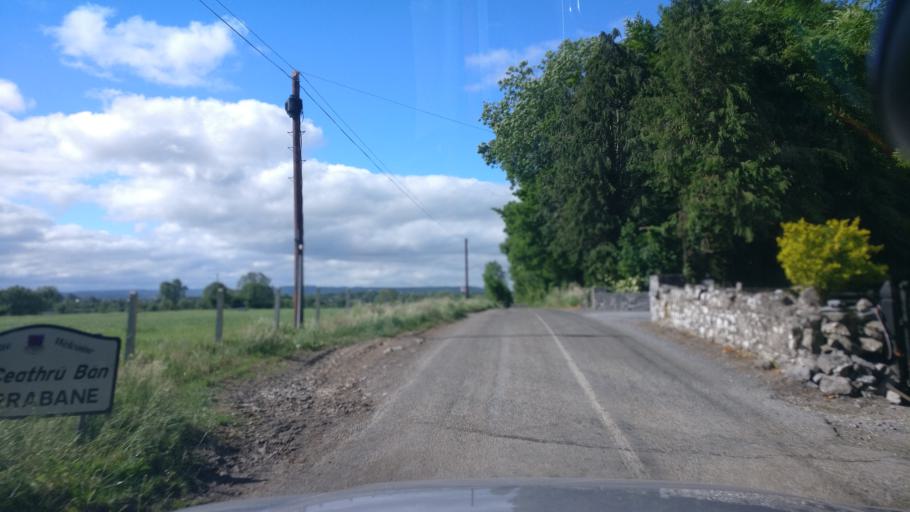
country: IE
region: Connaught
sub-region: County Galway
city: Loughrea
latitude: 53.2334
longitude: -8.6252
